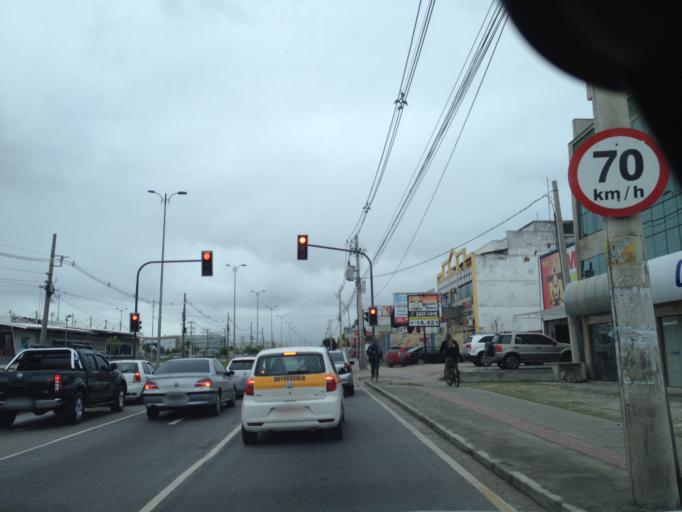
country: BR
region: Rio de Janeiro
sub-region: Nilopolis
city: Nilopolis
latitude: -23.0150
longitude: -43.4677
